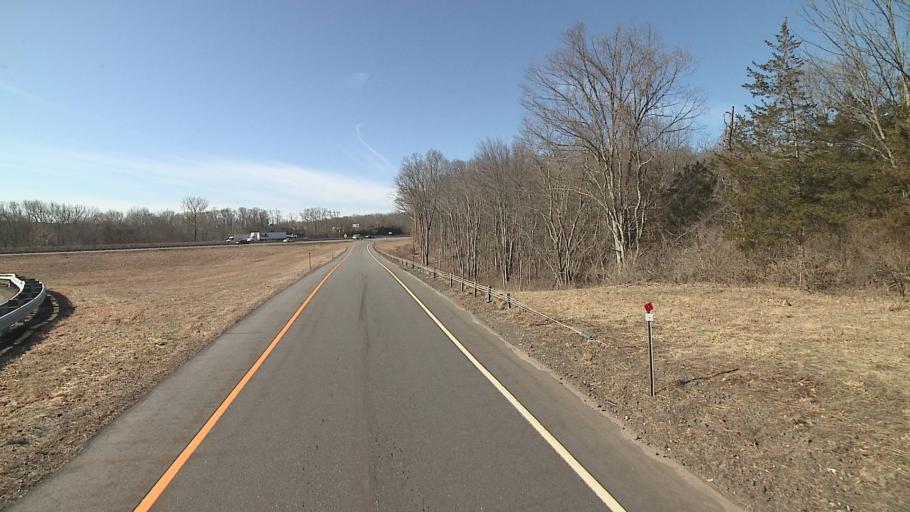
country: US
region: Connecticut
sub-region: New London County
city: Colchester
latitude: 41.5925
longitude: -72.3954
